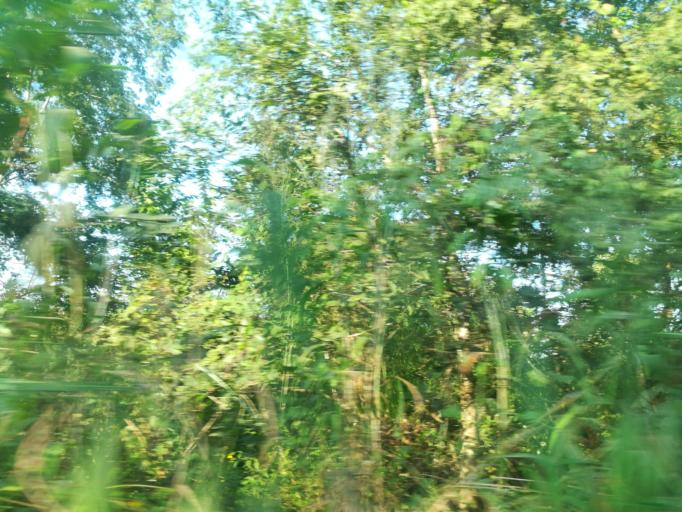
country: NG
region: Ogun
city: Abeokuta
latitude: 7.2029
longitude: 3.2156
